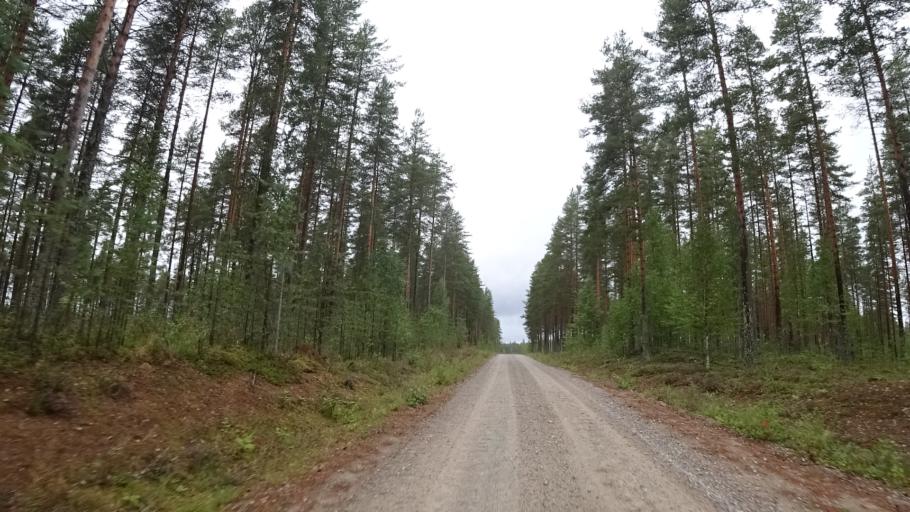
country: FI
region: North Karelia
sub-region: Pielisen Karjala
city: Lieksa
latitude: 63.5305
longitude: 30.0643
